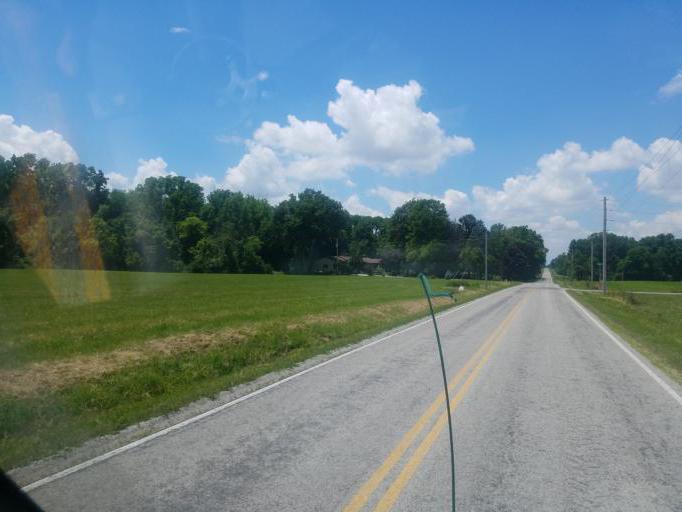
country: US
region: Ohio
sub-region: Huron County
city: Plymouth
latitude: 41.0679
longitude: -82.6217
